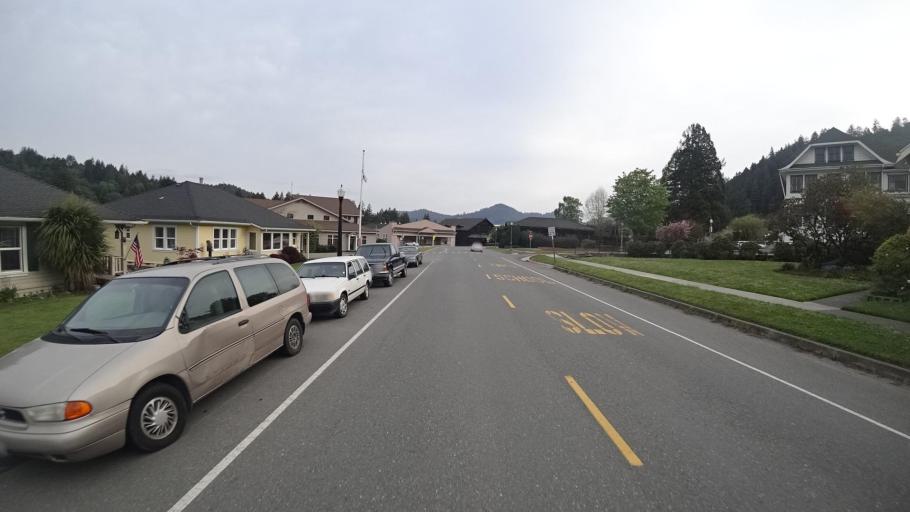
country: US
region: California
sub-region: Humboldt County
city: Rio Dell
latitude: 40.4828
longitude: -124.1029
